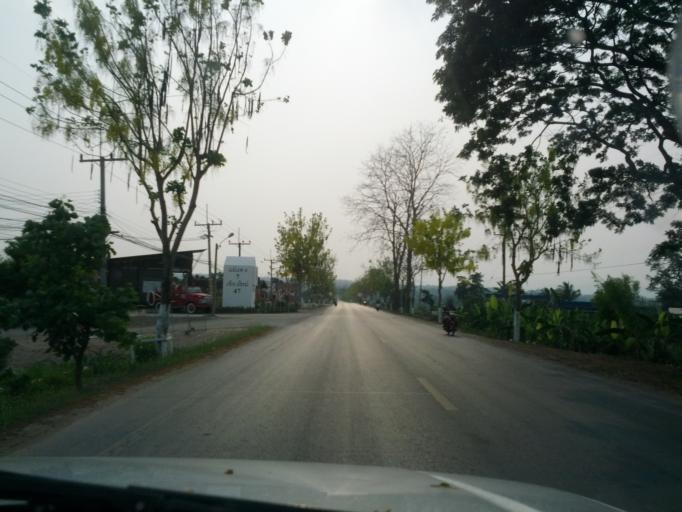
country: TH
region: Chiang Mai
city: Mae Taeng
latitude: 19.1447
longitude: 98.9965
